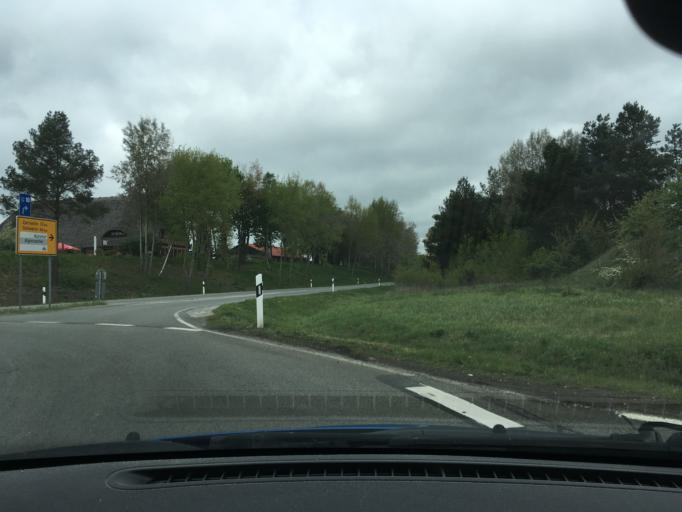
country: DE
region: Mecklenburg-Vorpommern
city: Wittenburg
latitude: 53.4991
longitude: 11.0951
